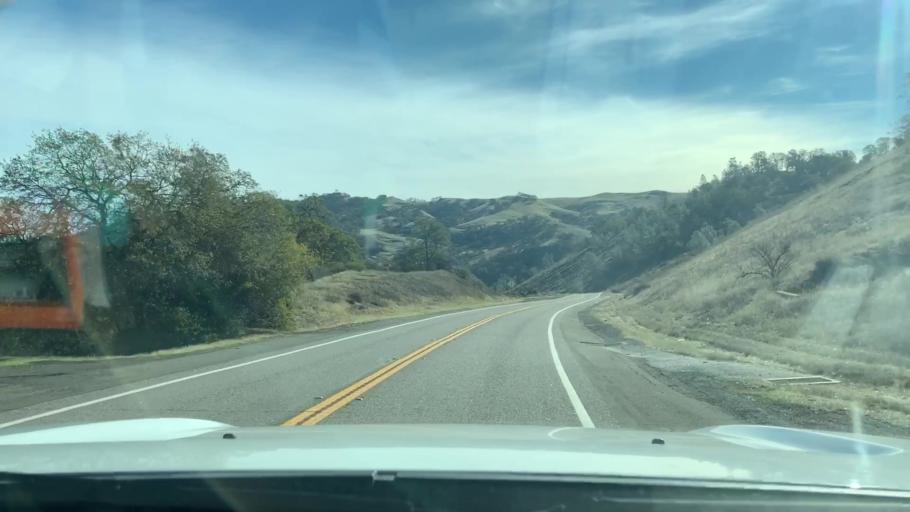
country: US
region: California
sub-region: Monterey County
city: King City
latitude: 36.1925
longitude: -120.7579
